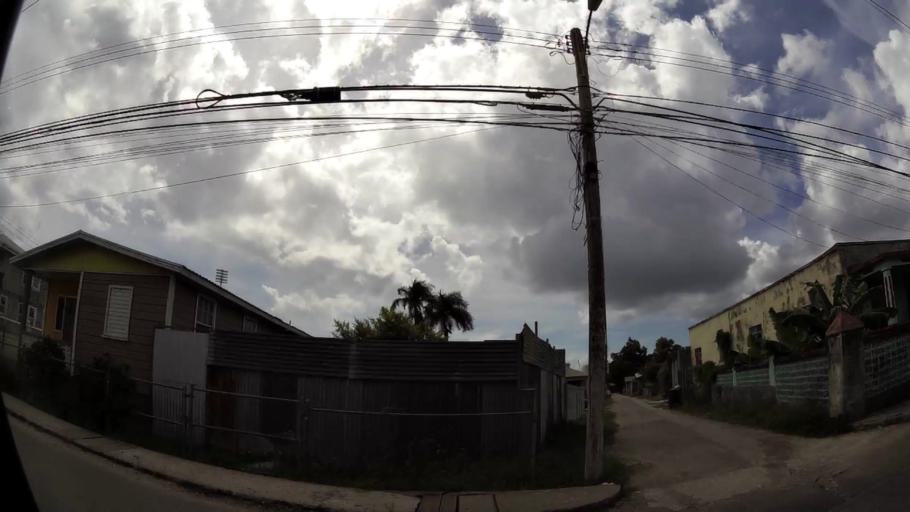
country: BB
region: Saint Michael
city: Bridgetown
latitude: 13.1078
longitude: -59.6213
